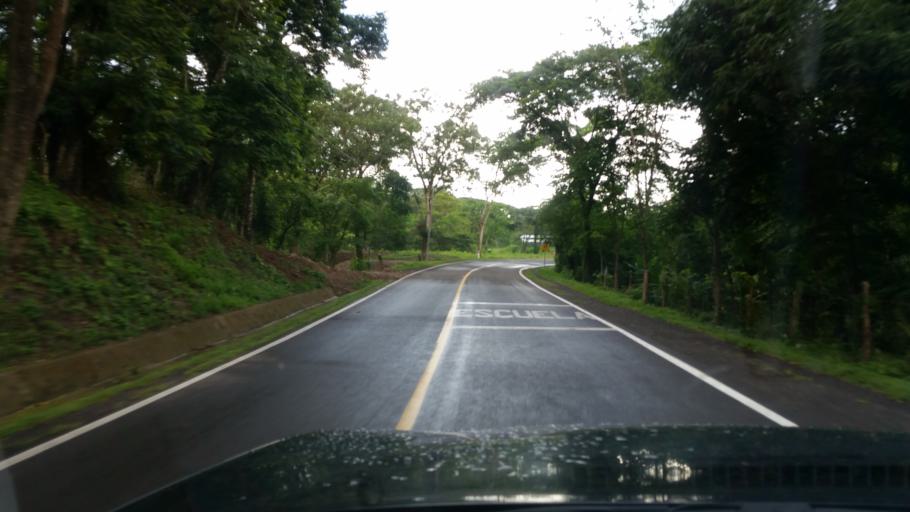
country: NI
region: Matagalpa
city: San Ramon
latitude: 13.0568
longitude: -85.7535
